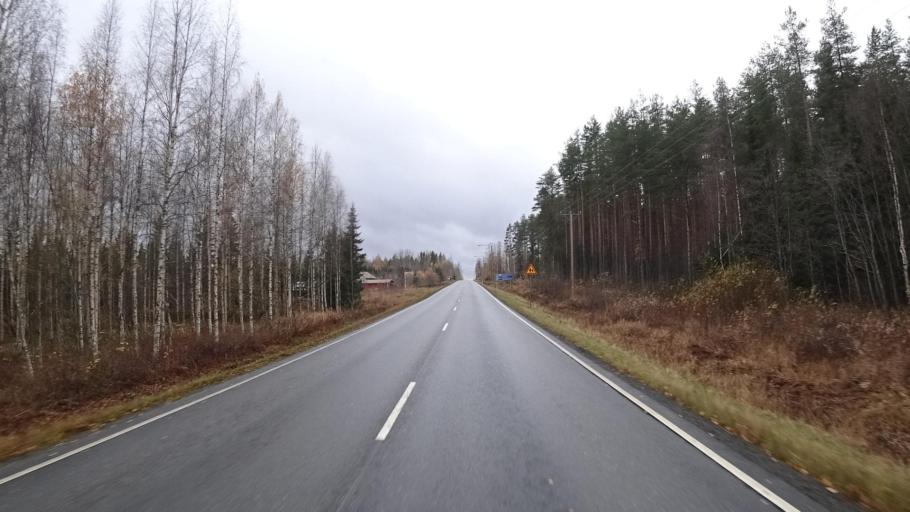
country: FI
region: Southern Savonia
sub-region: Mikkeli
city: Kangasniemi
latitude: 62.1756
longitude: 26.8640
